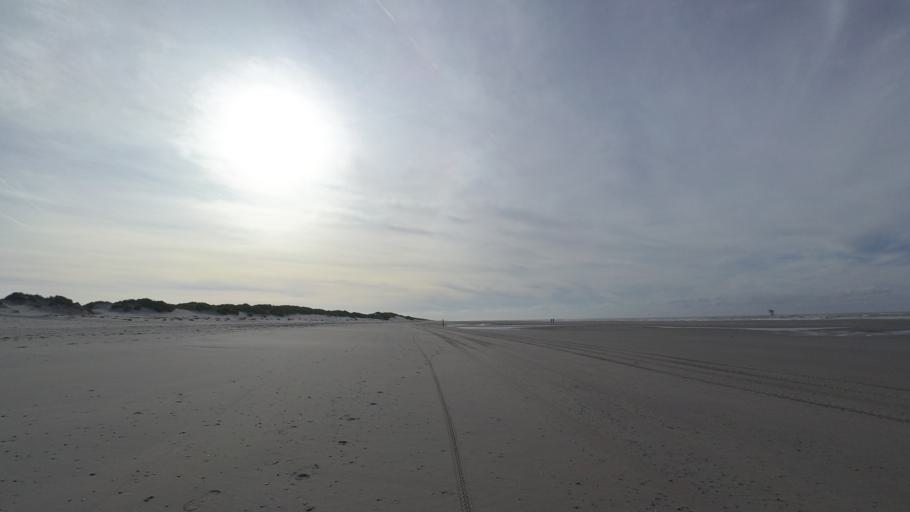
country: NL
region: Friesland
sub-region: Gemeente Dongeradeel
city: Holwerd
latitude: 53.4675
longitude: 5.9049
